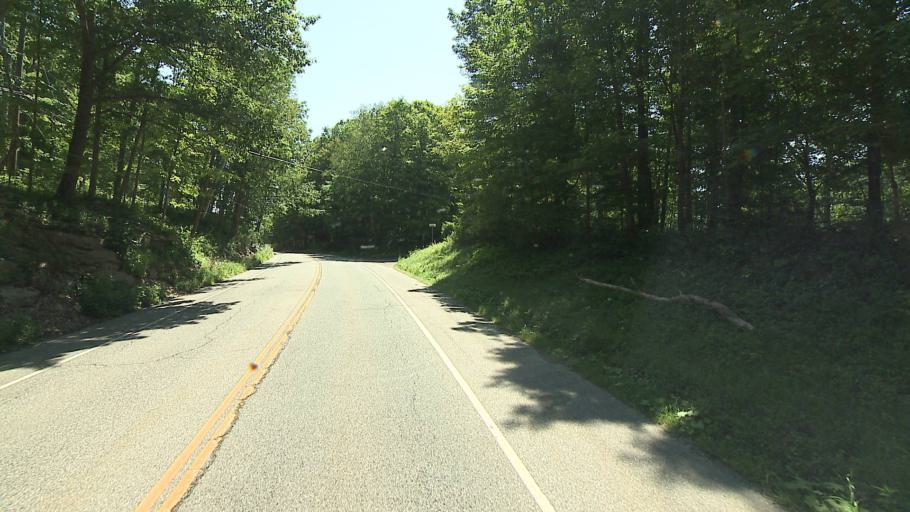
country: US
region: Connecticut
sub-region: Litchfield County
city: Kent
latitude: 41.8438
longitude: -73.4411
